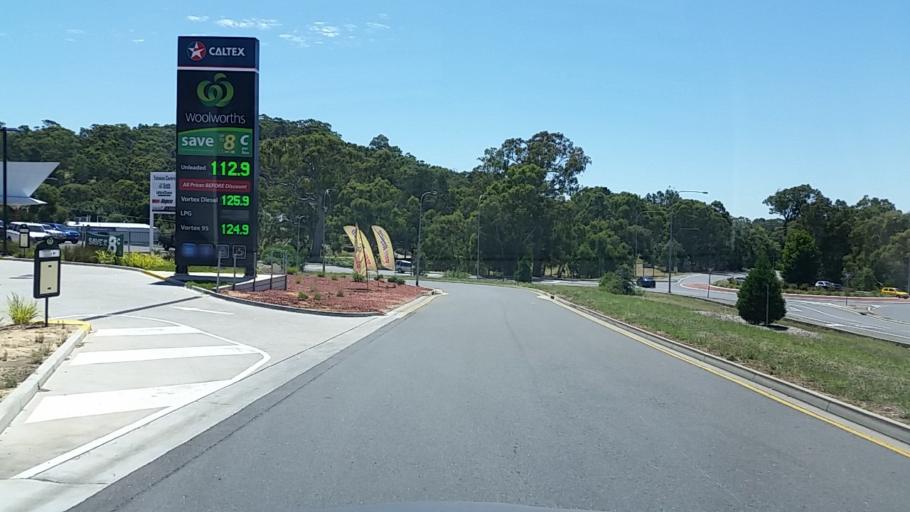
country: AU
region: South Australia
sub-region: Mount Barker
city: Little Hampton
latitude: -35.0558
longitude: 138.8522
